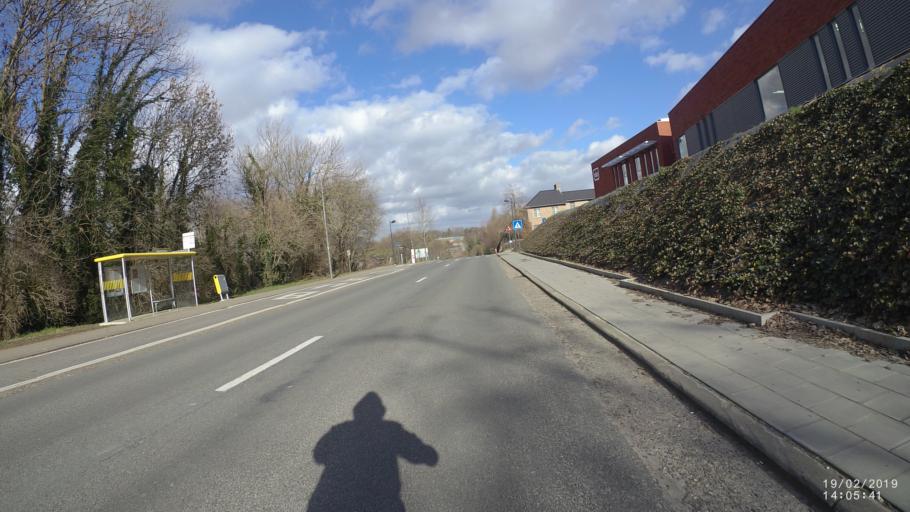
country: BE
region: Flanders
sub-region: Provincie Limburg
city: Tongeren
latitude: 50.7806
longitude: 5.4554
